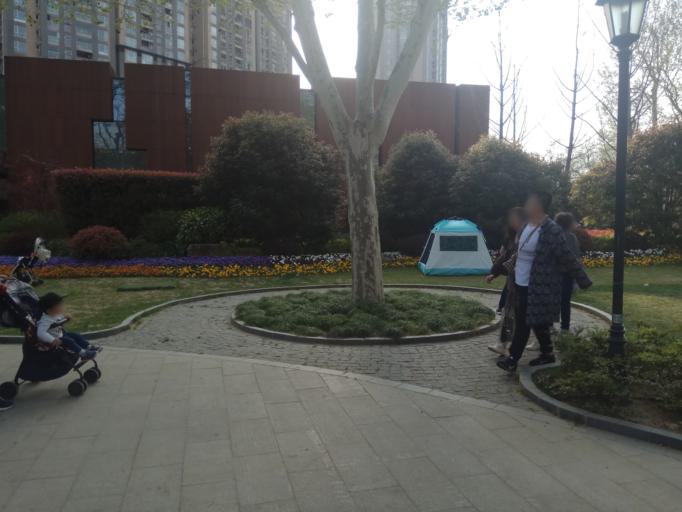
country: CN
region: Shanghai Shi
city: Changning
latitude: 31.2224
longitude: 121.4151
